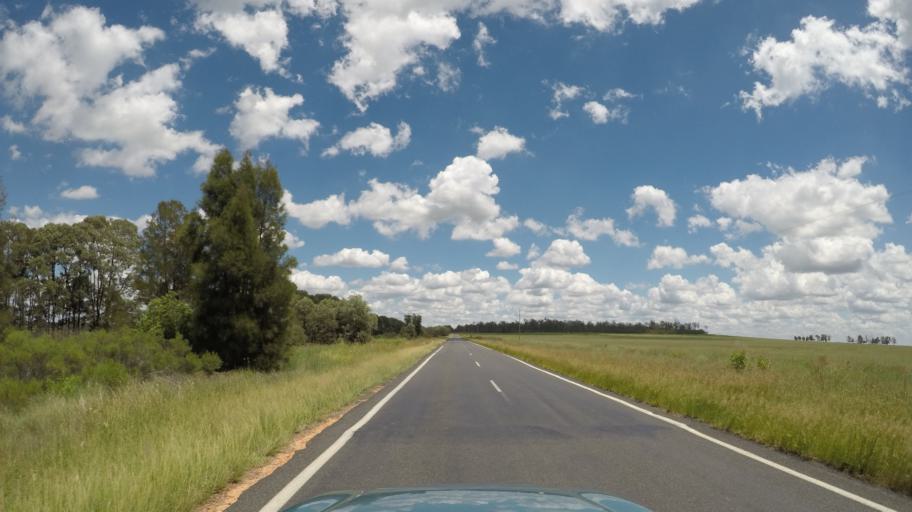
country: AU
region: Queensland
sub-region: Goondiwindi
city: Goondiwindi
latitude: -28.0064
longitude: 150.9162
